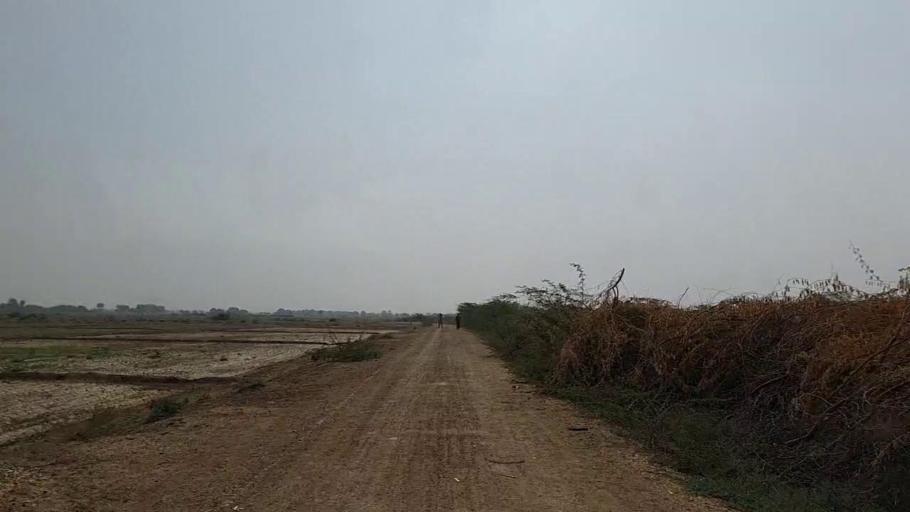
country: PK
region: Sindh
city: Naukot
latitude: 24.8111
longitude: 69.3614
